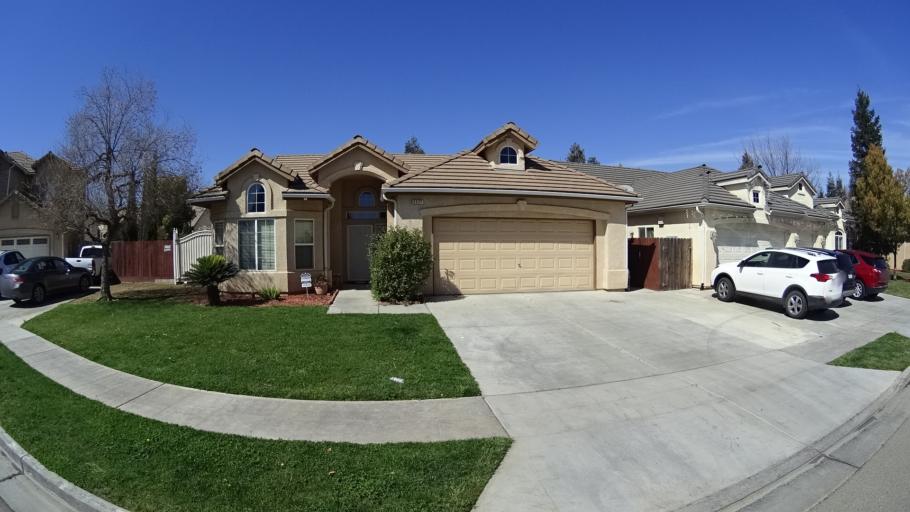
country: US
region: California
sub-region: Fresno County
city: Biola
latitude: 36.8160
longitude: -119.9027
